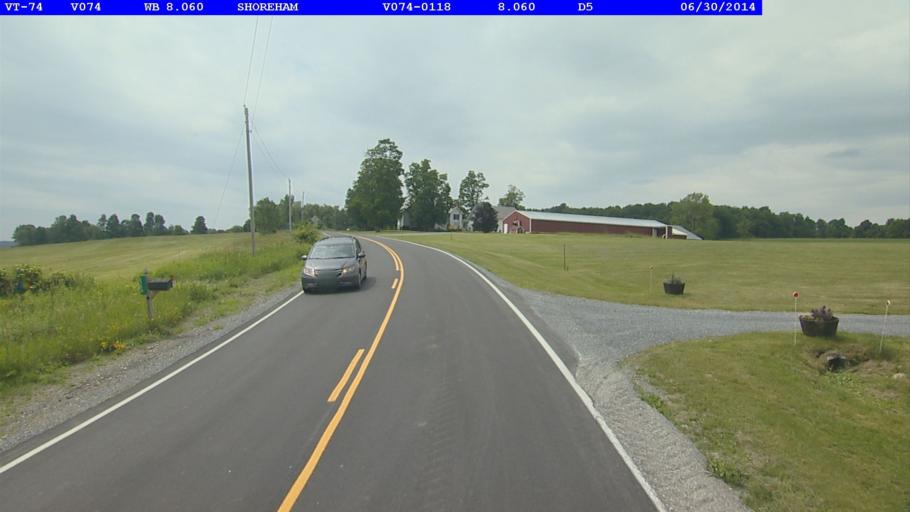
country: US
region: Vermont
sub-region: Addison County
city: Middlebury (village)
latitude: 43.9343
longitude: -73.2872
